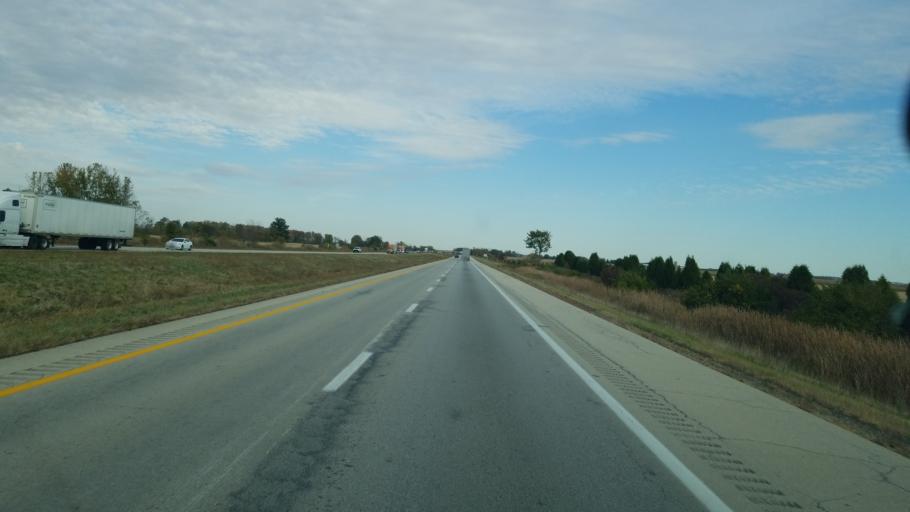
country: US
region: Ohio
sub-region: Clinton County
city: Wilmington
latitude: 39.5298
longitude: -83.8078
